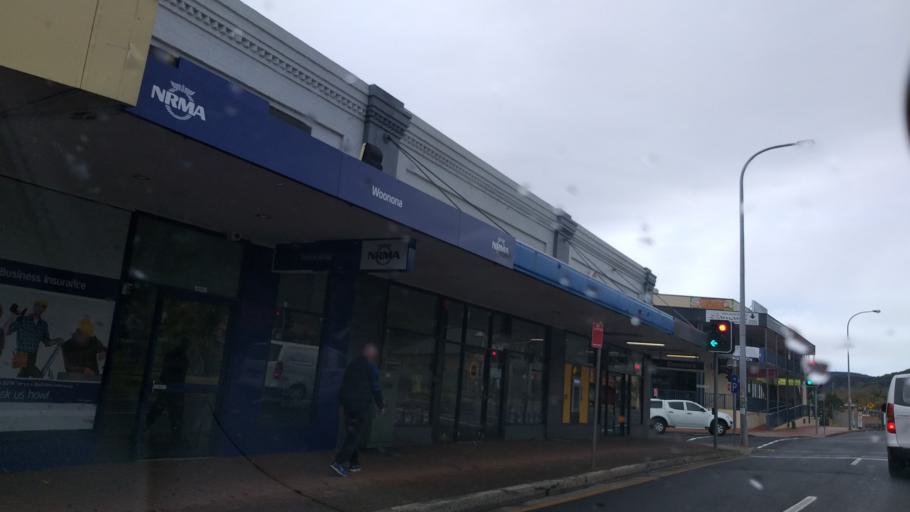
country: AU
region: New South Wales
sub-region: Wollongong
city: Bulli
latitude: -34.3421
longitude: 150.9056
